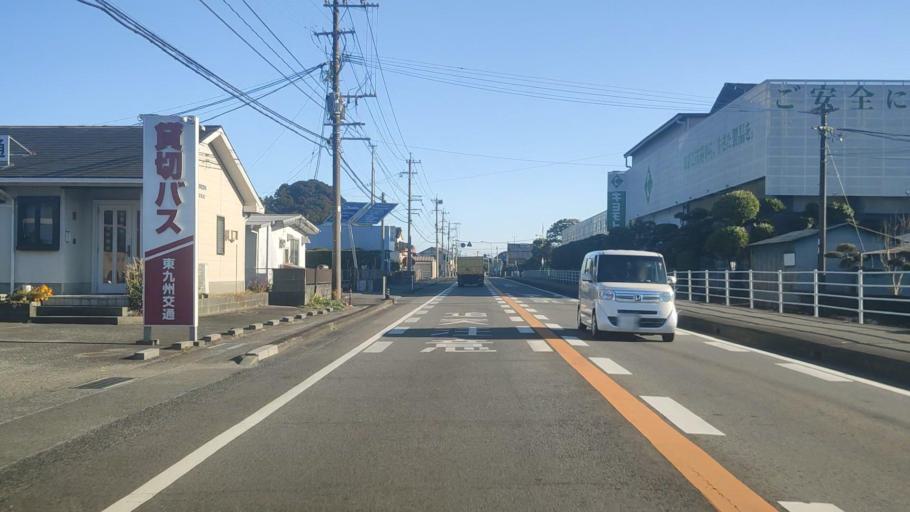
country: JP
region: Miyazaki
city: Nobeoka
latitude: 32.5068
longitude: 131.6747
